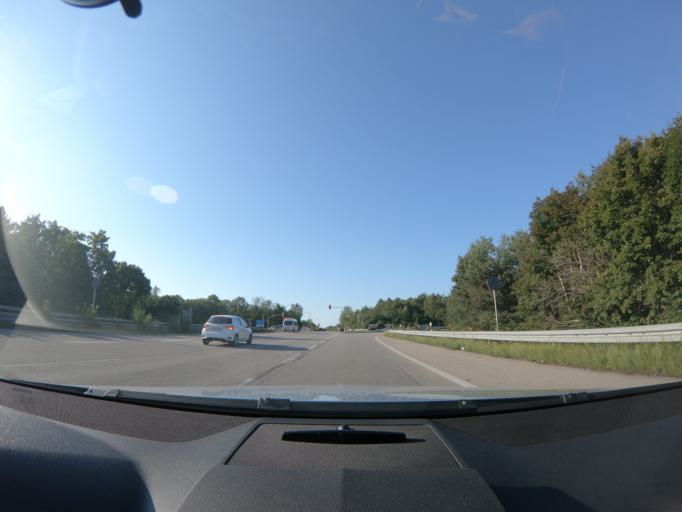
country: DE
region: Bavaria
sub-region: Upper Bavaria
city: Oberschleissheim
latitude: 48.2262
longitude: 11.5874
